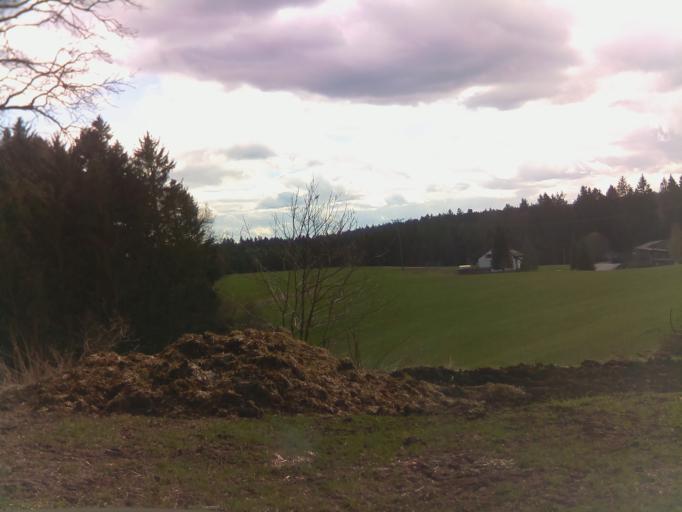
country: DE
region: Baden-Wuerttemberg
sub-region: Regierungsbezirk Stuttgart
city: Gschwend
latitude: 48.8979
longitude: 9.7007
